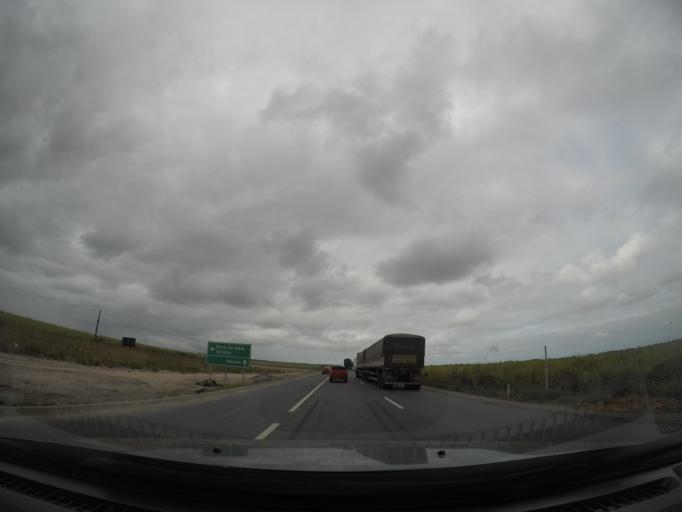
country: BR
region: Alagoas
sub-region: Pilar
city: Pilar
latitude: -9.6736
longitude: -36.0319
